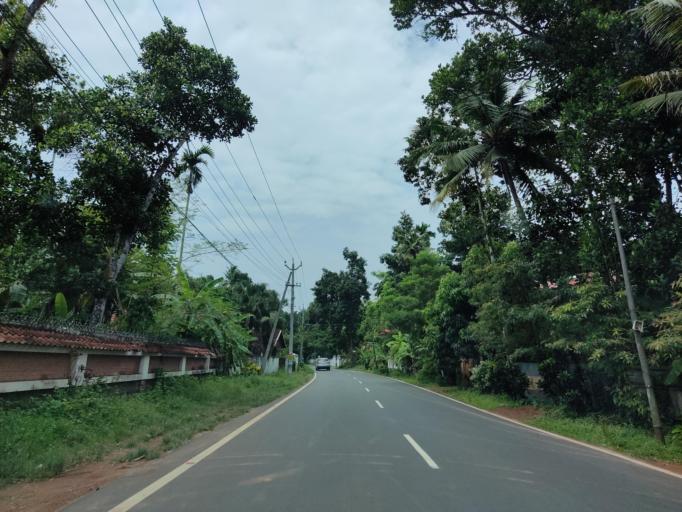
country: IN
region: Kerala
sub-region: Alappuzha
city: Chengannur
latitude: 9.2689
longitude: 76.6079
